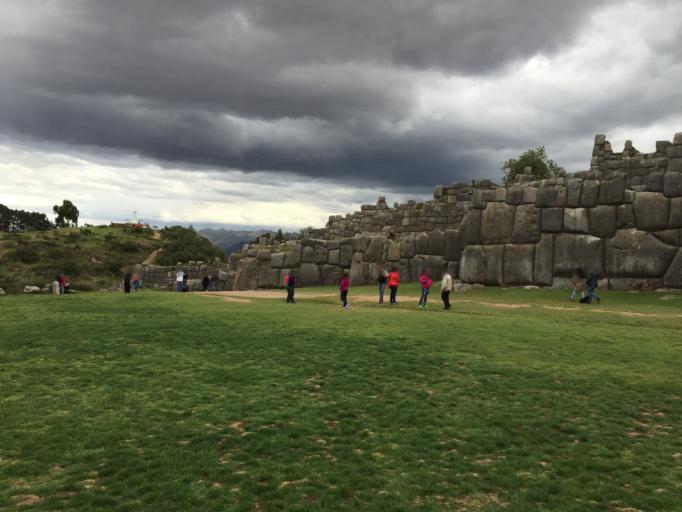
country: PE
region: Cusco
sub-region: Provincia de Cusco
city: Cusco
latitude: -13.5081
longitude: -71.9813
